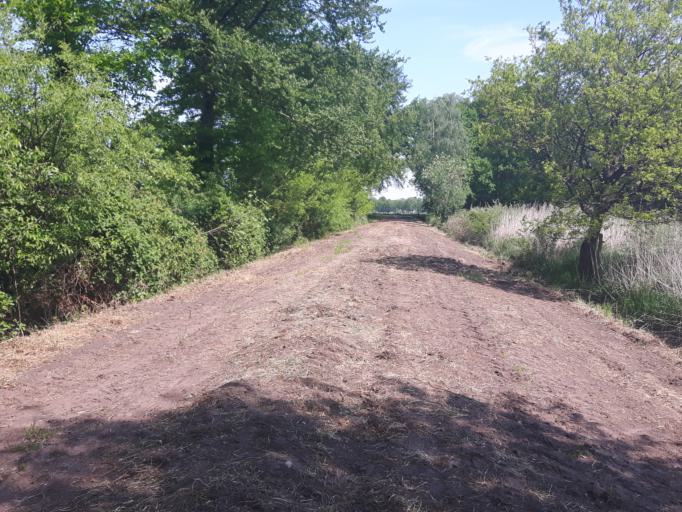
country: NL
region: Overijssel
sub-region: Gemeente Enschede
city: Enschede
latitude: 52.1662
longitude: 6.8574
